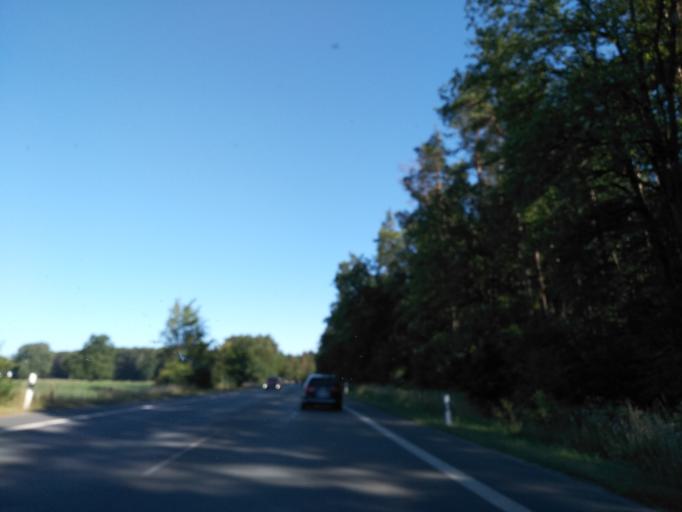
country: DE
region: Bavaria
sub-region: Regierungsbezirk Mittelfranken
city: Hessdorf
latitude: 49.6216
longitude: 10.9496
